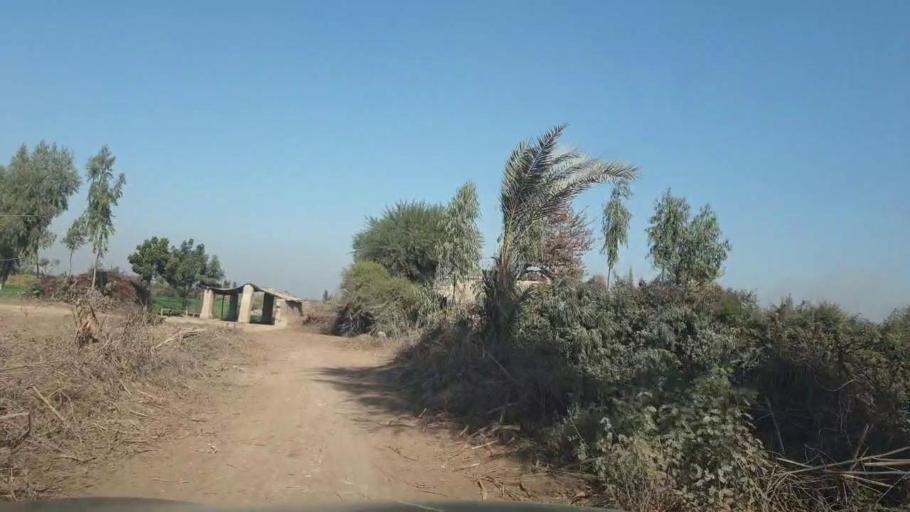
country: PK
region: Sindh
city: Mirpur Mathelo
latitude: 28.0983
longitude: 69.5272
